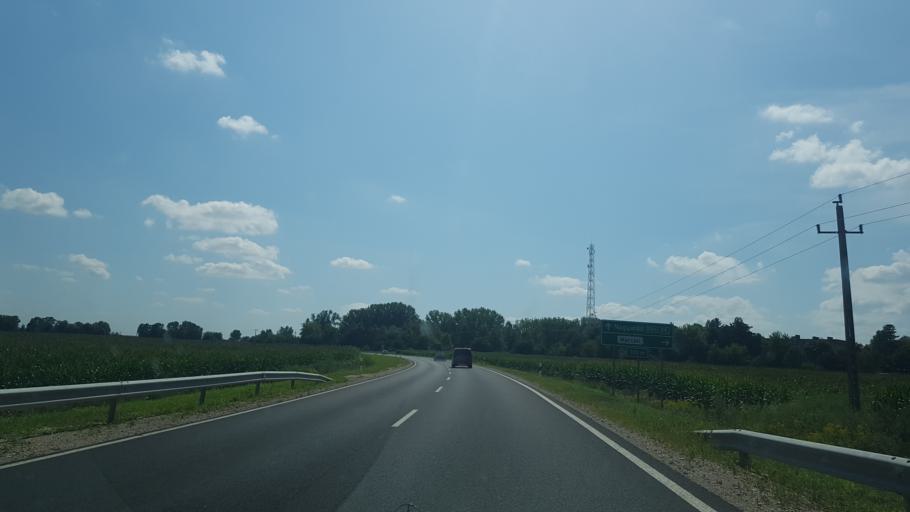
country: HU
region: Somogy
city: Marcali
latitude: 46.5627
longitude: 17.4143
